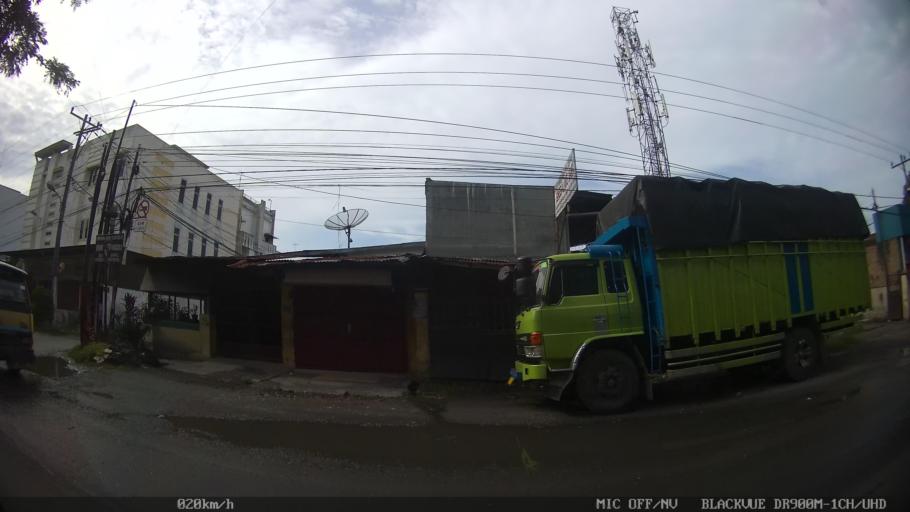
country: ID
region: North Sumatra
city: Medan
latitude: 3.6287
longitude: 98.6986
